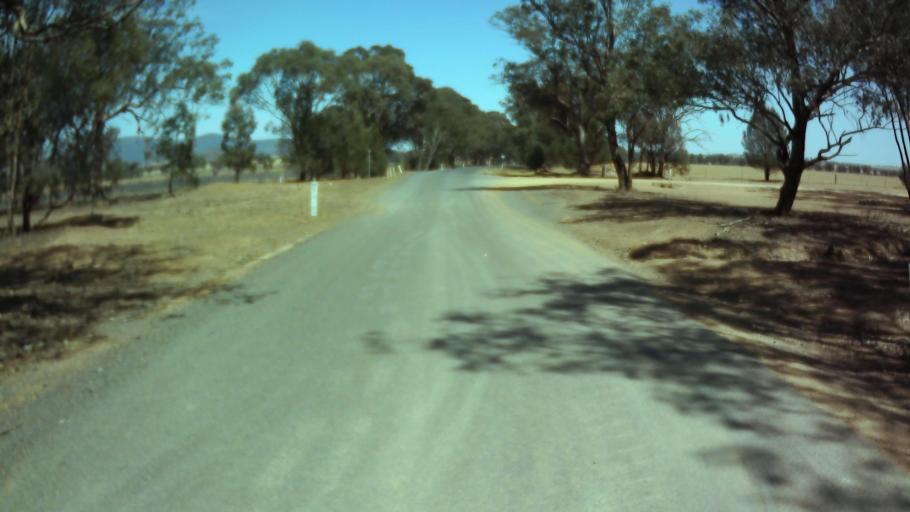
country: AU
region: New South Wales
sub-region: Weddin
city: Grenfell
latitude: -33.8704
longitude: 148.0885
